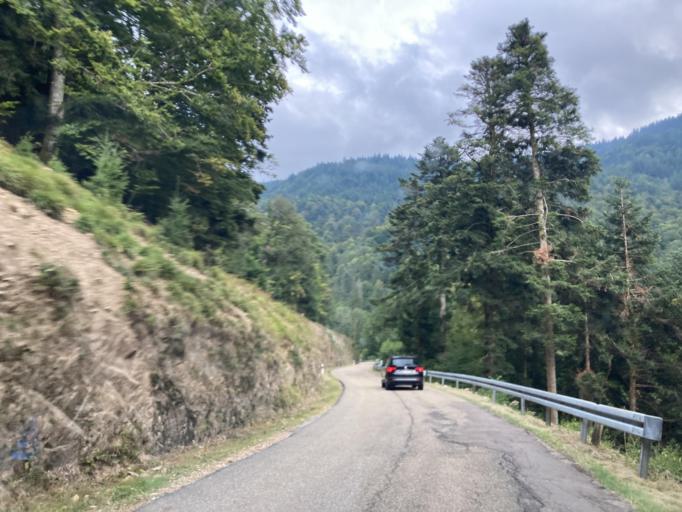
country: DE
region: Baden-Wuerttemberg
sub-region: Freiburg Region
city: Sulzburg
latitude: 47.8034
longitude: 7.7290
